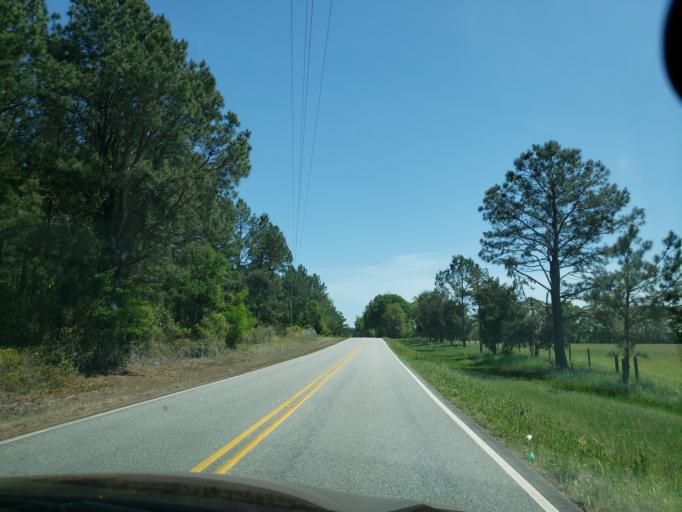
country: US
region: Alabama
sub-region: Tallapoosa County
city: Camp Hill
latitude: 32.7004
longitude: -85.6575
